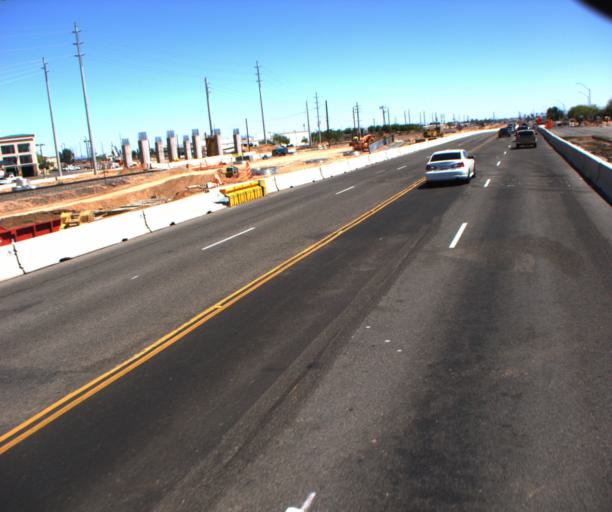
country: US
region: Arizona
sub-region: Maricopa County
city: Surprise
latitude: 33.6390
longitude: -112.3508
